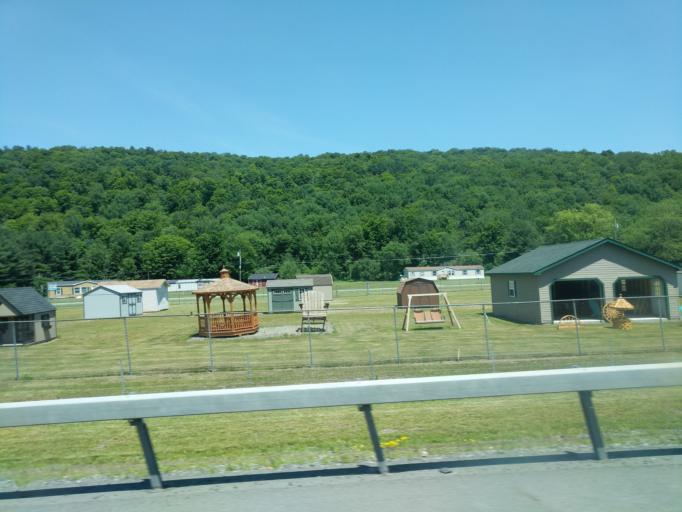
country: US
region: New York
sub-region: Sullivan County
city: Livingston Manor
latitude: 41.8653
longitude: -74.7887
